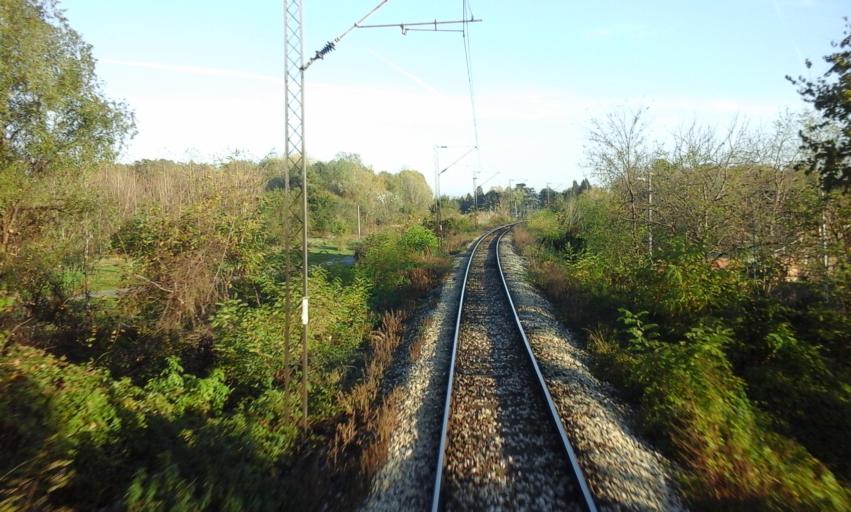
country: RS
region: Autonomna Pokrajina Vojvodina
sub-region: Juznobacki Okrug
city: Petrovaradin
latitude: 45.2559
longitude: 19.8761
